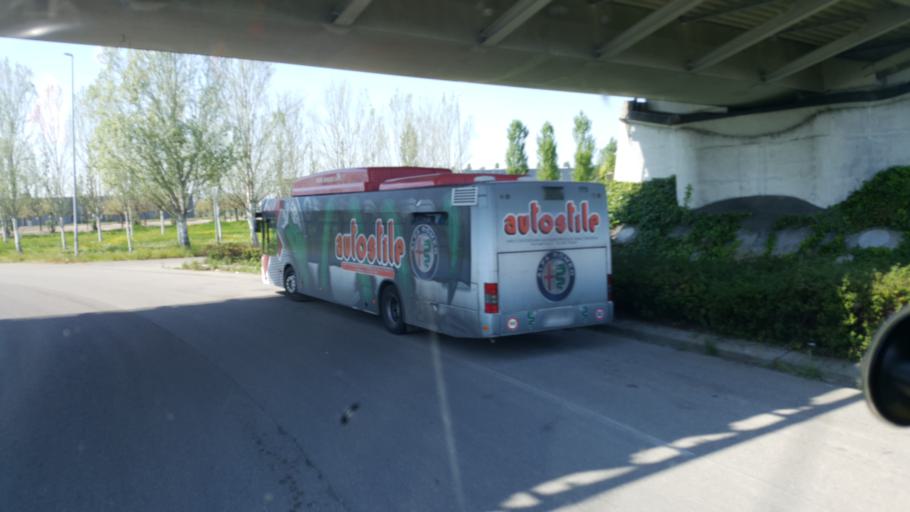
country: IT
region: Emilia-Romagna
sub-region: Provincia di Reggio Emilia
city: Reggio nell'Emilia
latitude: 44.7311
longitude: 10.6397
